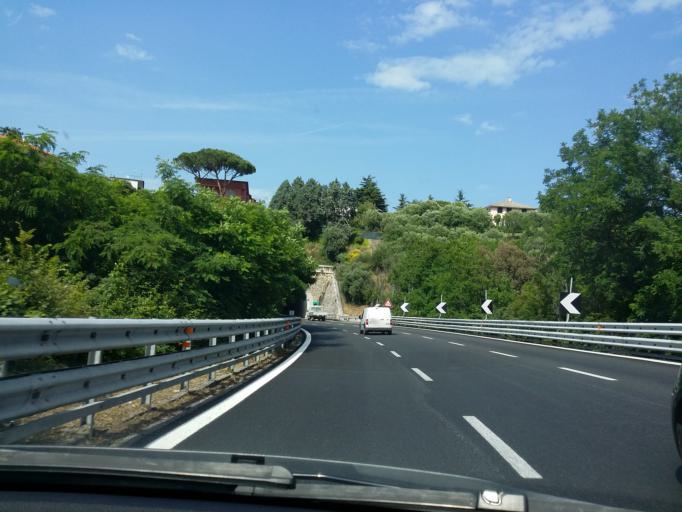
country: IT
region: Liguria
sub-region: Provincia di Savona
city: Celle Ligure
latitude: 44.3357
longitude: 8.5322
